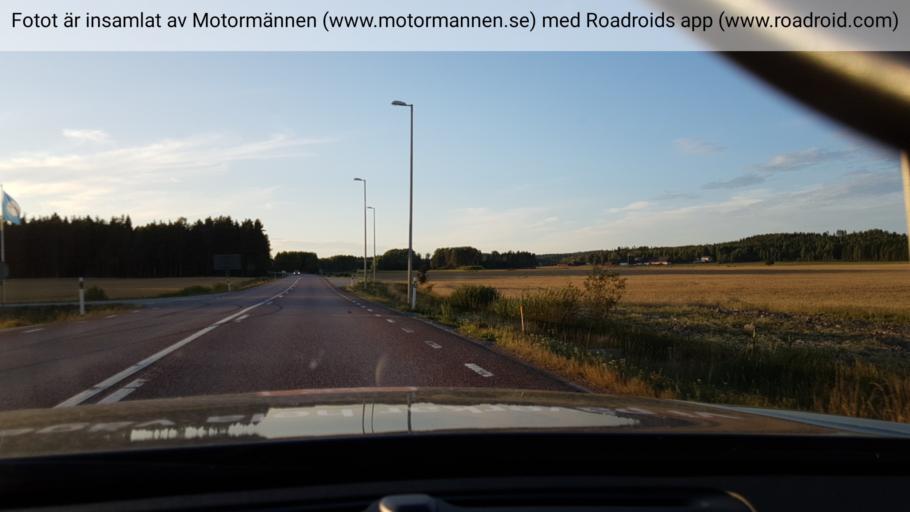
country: SE
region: OErebro
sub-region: Karlskoga Kommun
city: Karlskoga
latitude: 59.4030
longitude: 14.4323
